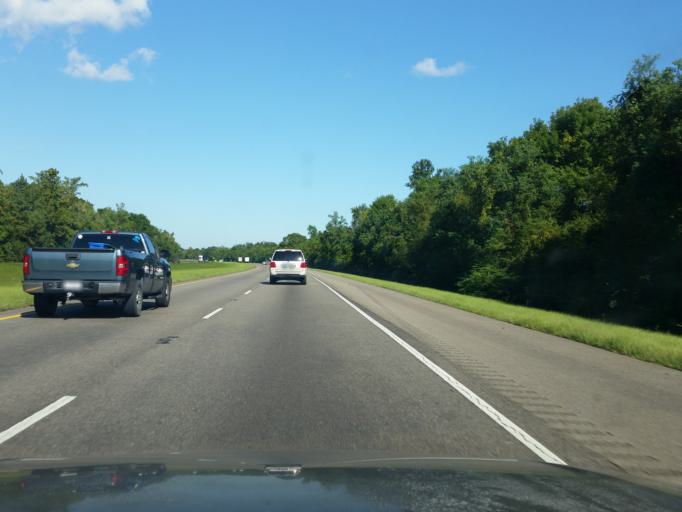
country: US
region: Mississippi
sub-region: Hancock County
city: Pearlington
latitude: 30.2966
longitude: -89.6758
